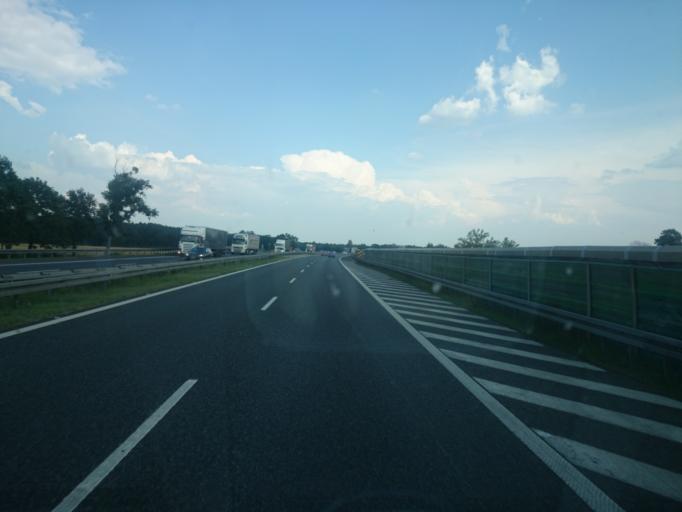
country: PL
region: Opole Voivodeship
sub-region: Powiat brzeski
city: Lewin Brzeski
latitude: 50.7093
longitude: 17.6010
